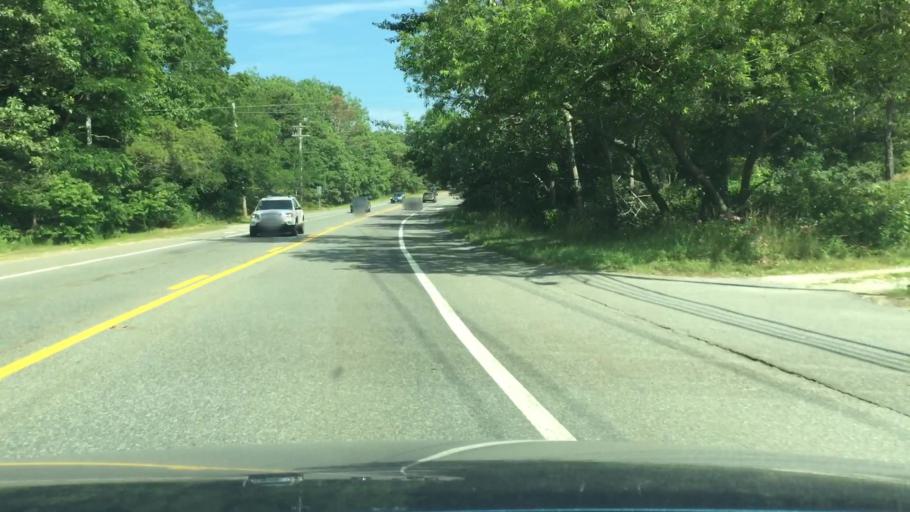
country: US
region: Massachusetts
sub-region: Barnstable County
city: Truro
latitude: 42.0039
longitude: -70.0552
